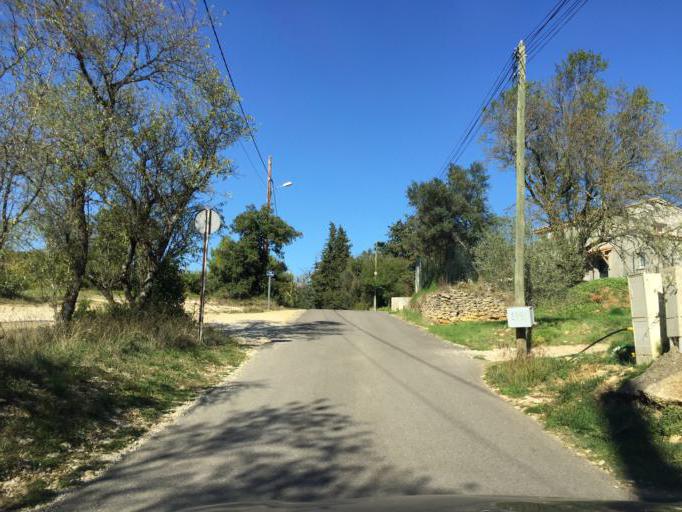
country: FR
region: Provence-Alpes-Cote d'Azur
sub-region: Departement du Vaucluse
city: Piolenc
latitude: 44.1955
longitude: 4.7531
